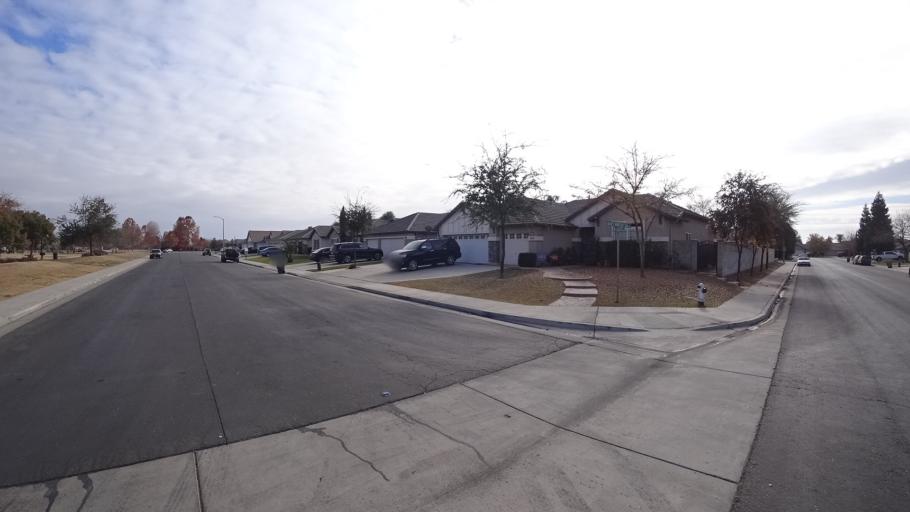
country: US
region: California
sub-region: Kern County
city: Greenacres
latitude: 35.3020
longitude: -119.1218
